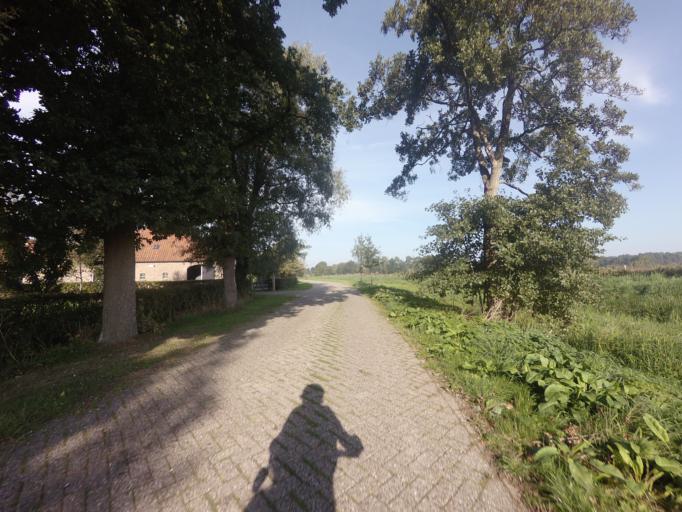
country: NL
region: Groningen
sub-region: Gemeente Leek
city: Leek
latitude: 53.1493
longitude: 6.4686
